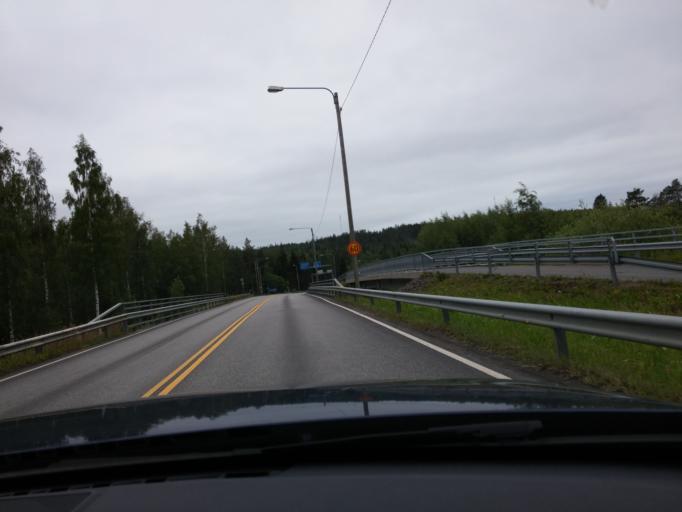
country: FI
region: Central Finland
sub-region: Saarijaervi-Viitasaari
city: Saarijaervi
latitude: 62.6881
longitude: 25.3191
